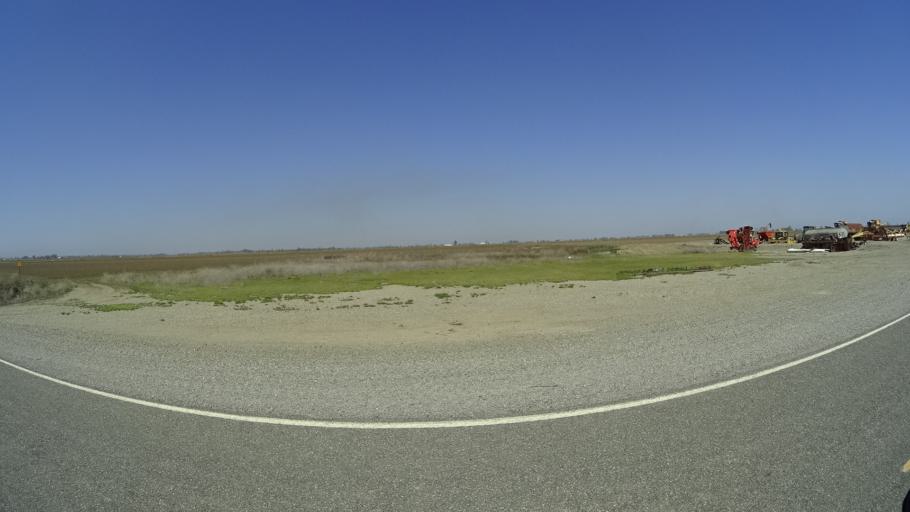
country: US
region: California
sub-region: Glenn County
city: Willows
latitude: 39.4947
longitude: -122.1476
